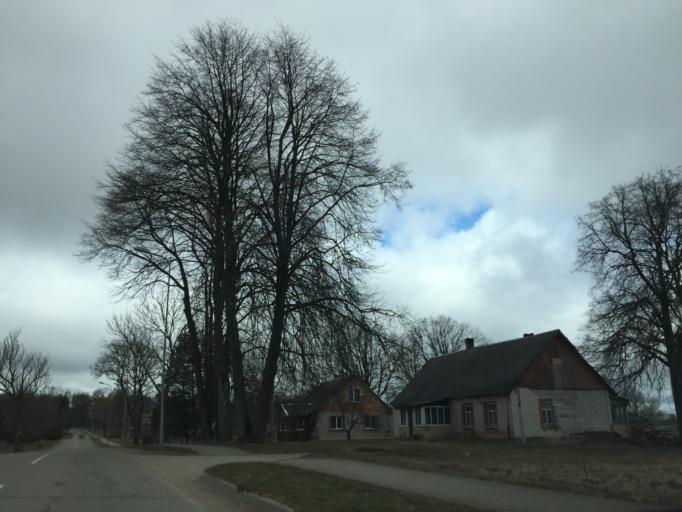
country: LV
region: Ilukste
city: Ilukste
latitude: 56.0677
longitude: 26.1425
